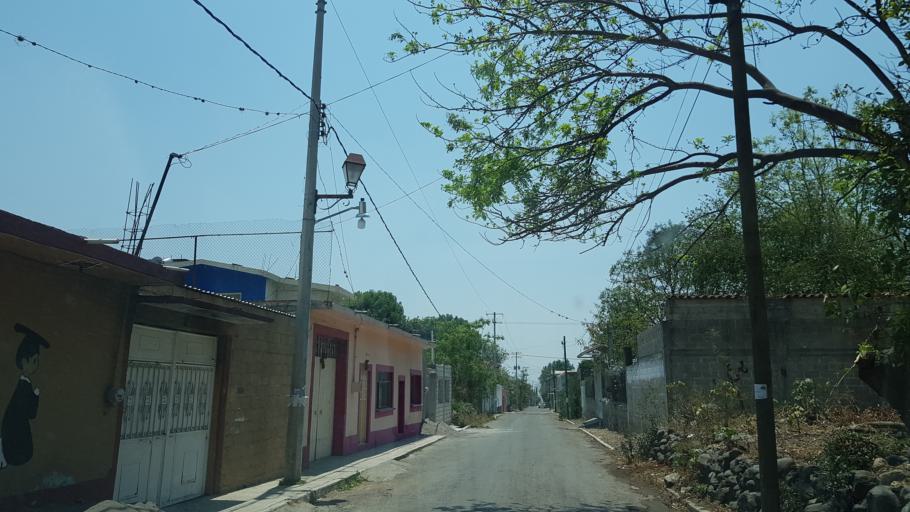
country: MX
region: Puebla
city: Huaquechula
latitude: 18.7754
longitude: -98.5453
